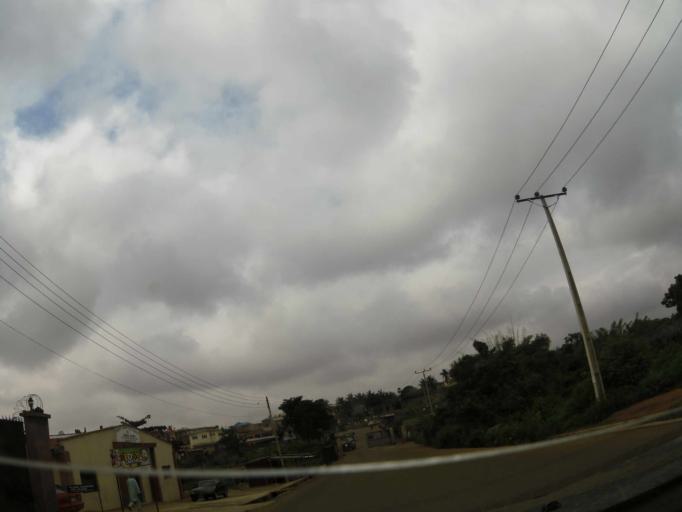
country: NG
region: Oyo
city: Ibadan
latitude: 7.4381
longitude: 3.9511
